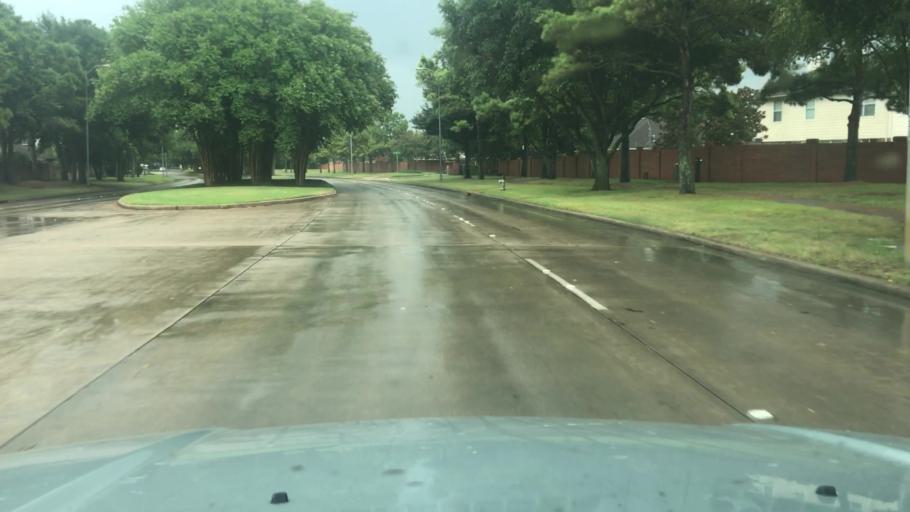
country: US
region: Texas
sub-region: Fort Bend County
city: Cinco Ranch
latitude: 29.7400
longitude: -95.7863
